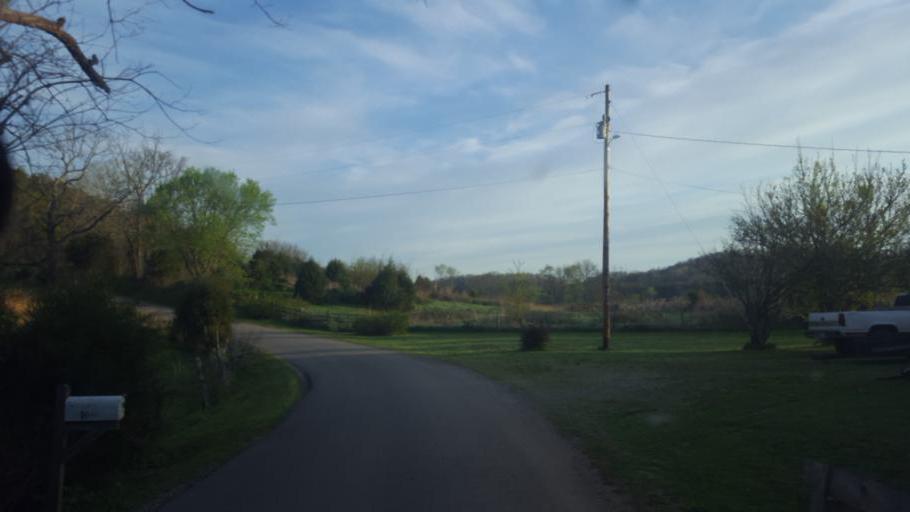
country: US
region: Kentucky
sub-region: Barren County
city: Cave City
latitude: 37.1870
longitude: -86.0117
